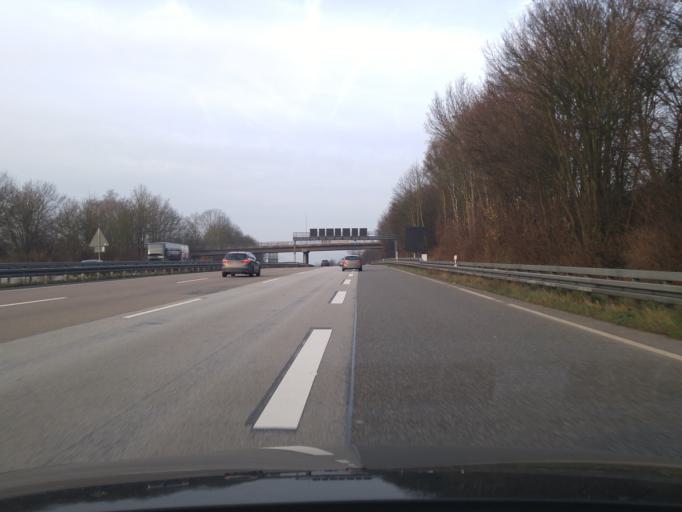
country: DE
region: Hesse
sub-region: Regierungsbezirk Giessen
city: Limburg an der Lahn
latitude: 50.4017
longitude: 8.0651
